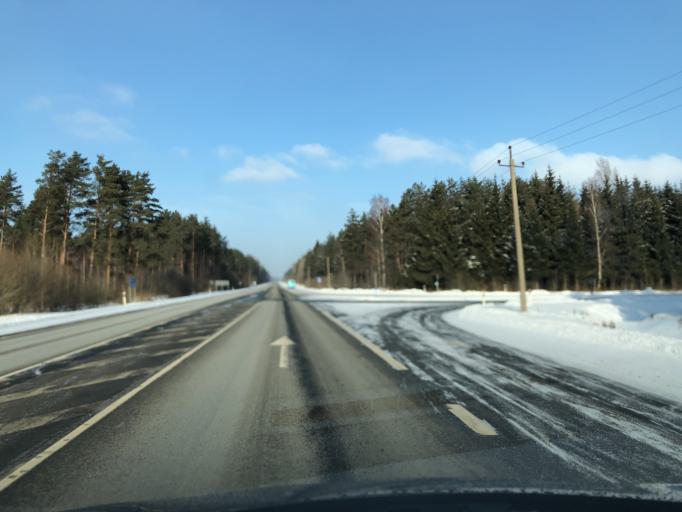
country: EE
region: Tartu
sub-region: Tartu linn
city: Tartu
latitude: 58.3864
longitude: 26.6696
